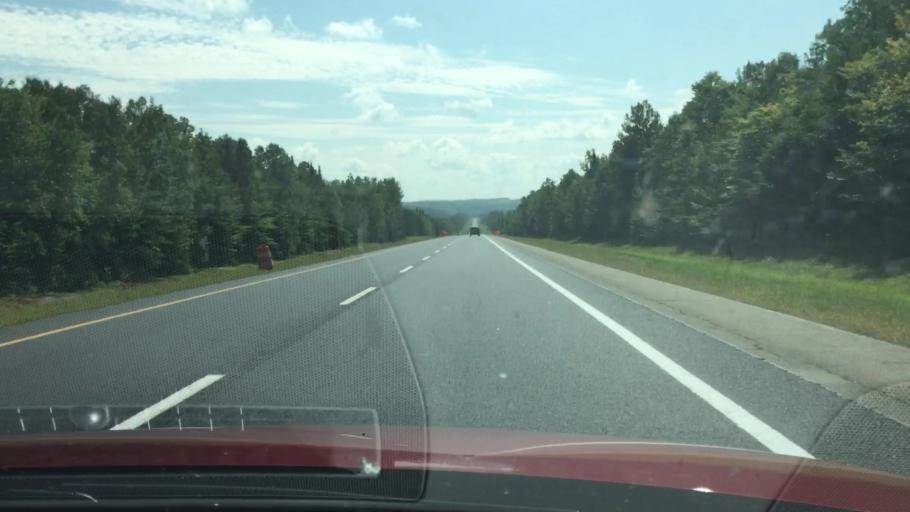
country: US
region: Maine
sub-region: Penobscot County
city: Patten
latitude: 45.8339
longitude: -68.4336
